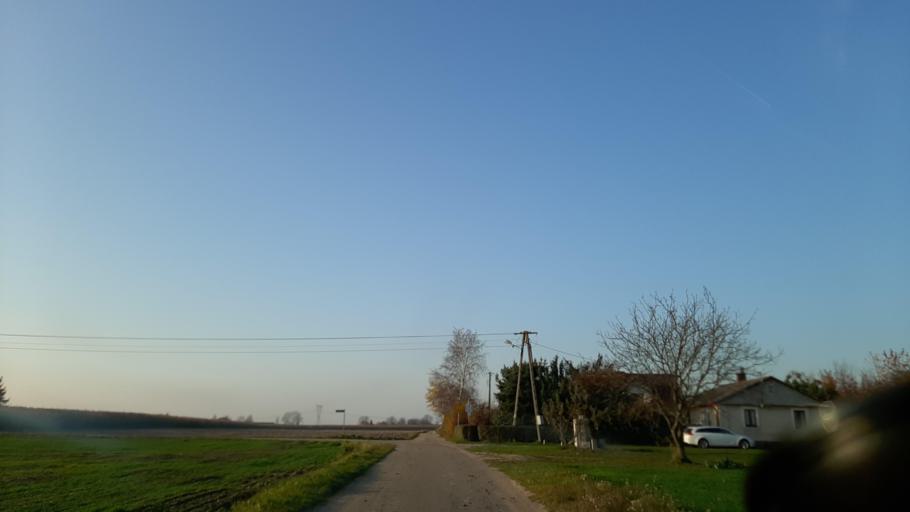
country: PL
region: Lublin Voivodeship
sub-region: Powiat lubelski
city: Garbow
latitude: 51.3735
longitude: 22.3519
